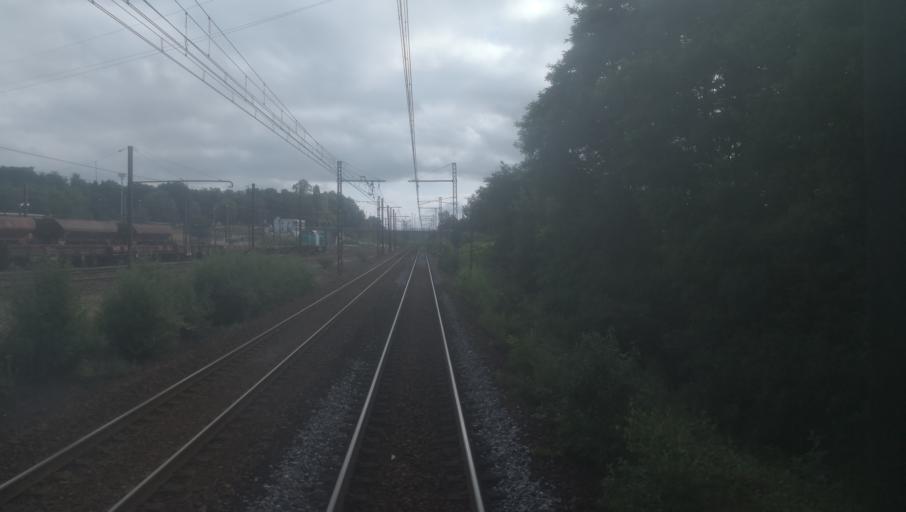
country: FR
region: Limousin
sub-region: Departement de la Haute-Vienne
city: Le Palais-sur-Vienne
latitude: 45.8486
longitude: 1.2938
